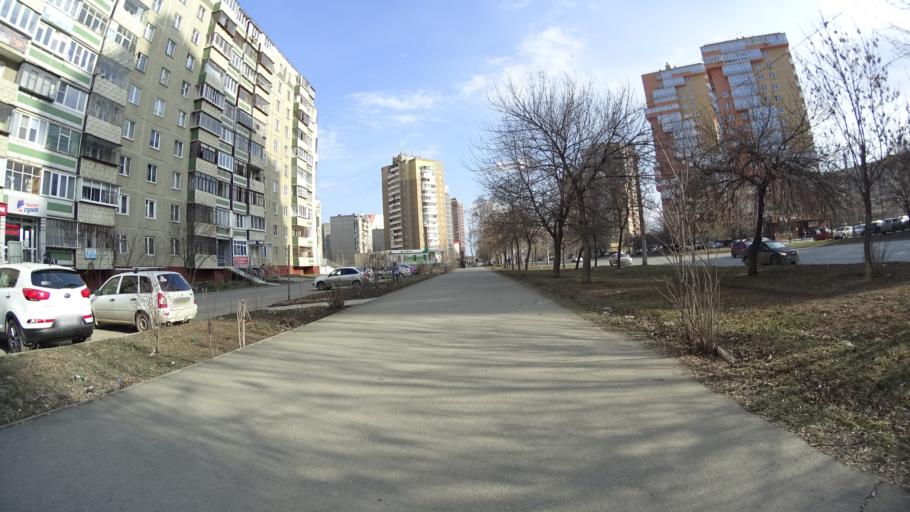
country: RU
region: Chelyabinsk
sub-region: Gorod Chelyabinsk
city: Chelyabinsk
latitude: 55.1772
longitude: 61.3003
